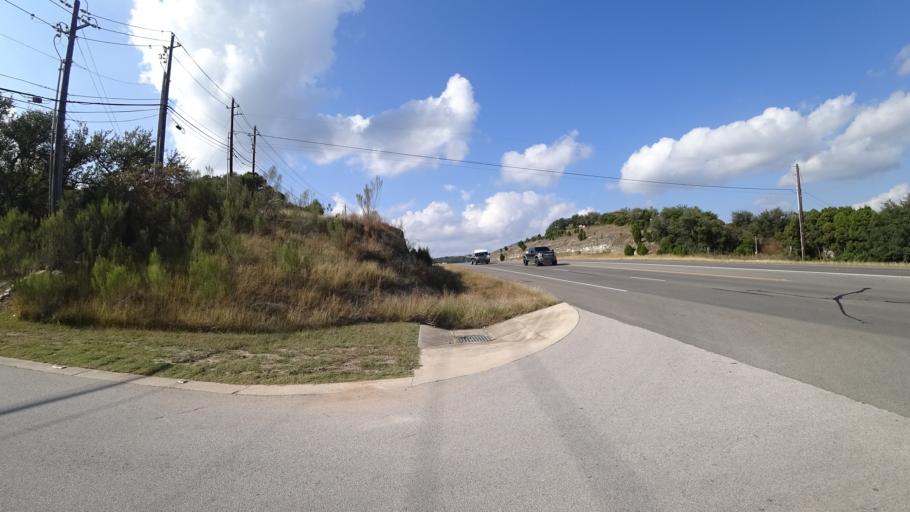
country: US
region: Texas
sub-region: Travis County
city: Lost Creek
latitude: 30.3146
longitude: -97.8559
